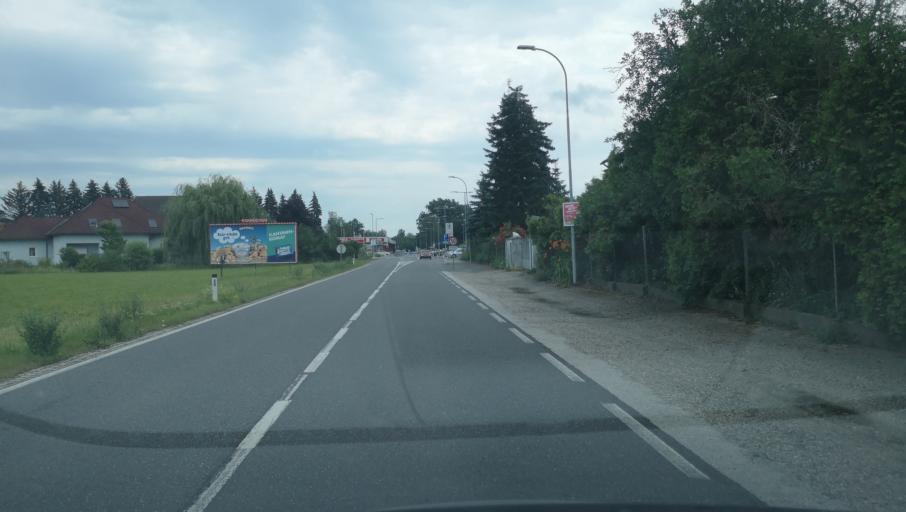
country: AT
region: Lower Austria
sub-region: Politischer Bezirk Melk
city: Klein-Poechlarn
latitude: 48.2178
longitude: 15.2129
